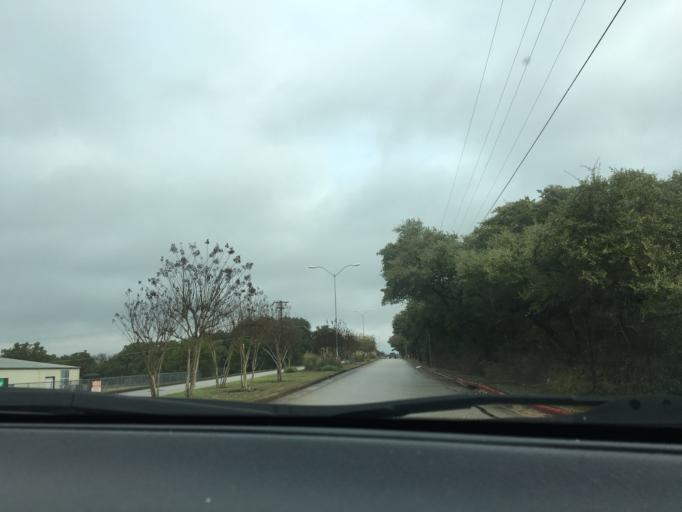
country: US
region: Texas
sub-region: Hays County
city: Dripping Springs
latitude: 30.1861
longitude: -98.0827
